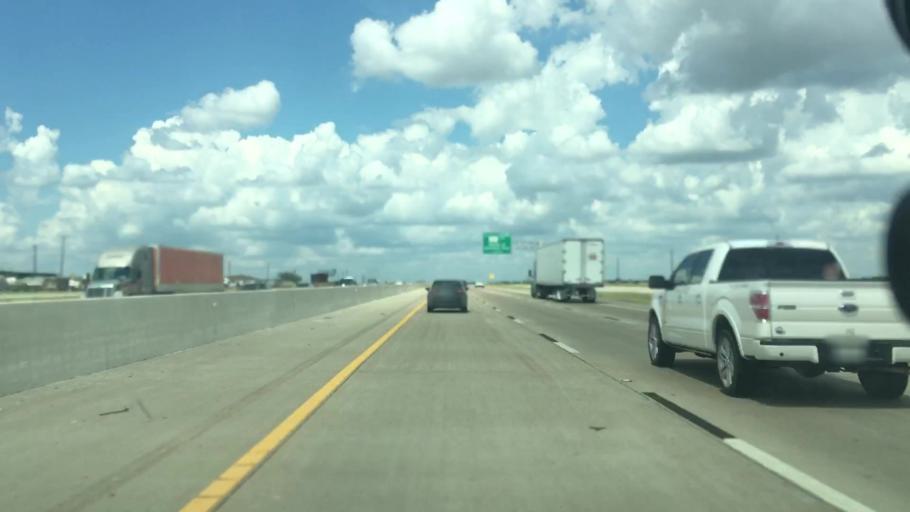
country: US
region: Texas
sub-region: McLennan County
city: Lorena
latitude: 31.3506
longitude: -97.2198
